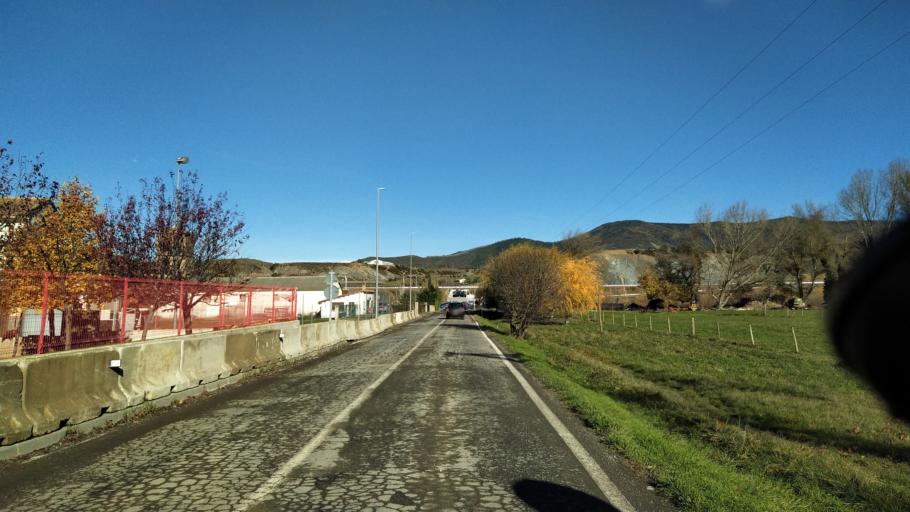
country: ES
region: Aragon
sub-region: Provincia de Huesca
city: Santa Cruz de la Seros
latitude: 42.5600
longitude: -0.7128
